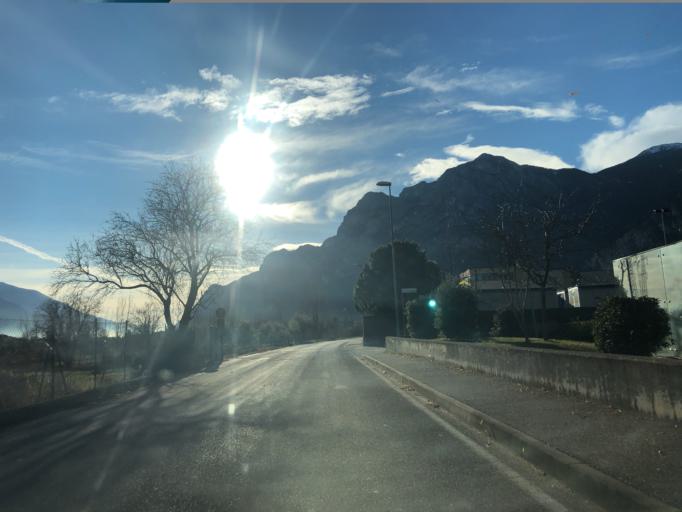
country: IT
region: Trentino-Alto Adige
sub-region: Provincia di Trento
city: Arco
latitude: 45.9120
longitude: 10.8655
